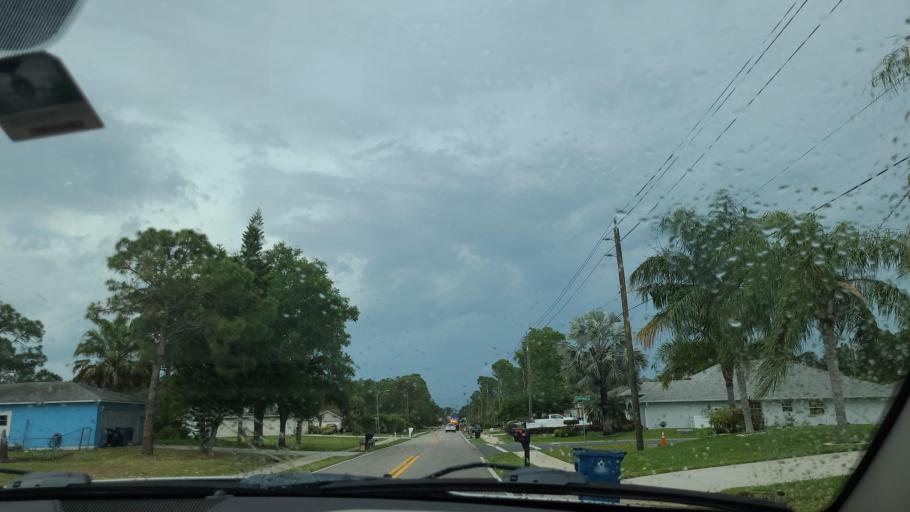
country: US
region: Florida
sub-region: Brevard County
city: Grant-Valkaria
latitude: 27.9524
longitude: -80.6411
